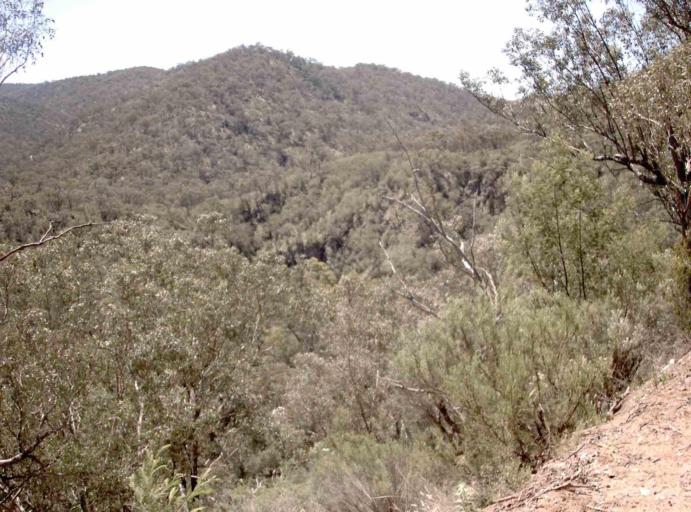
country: AU
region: New South Wales
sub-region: Snowy River
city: Jindabyne
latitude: -37.0468
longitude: 148.5402
